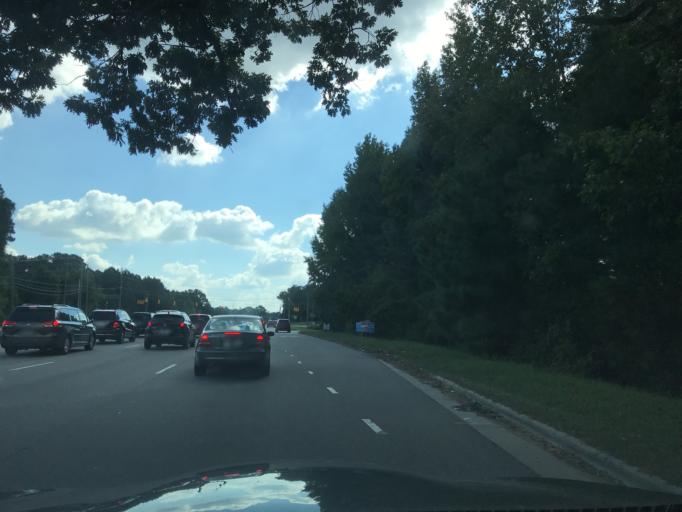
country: US
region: North Carolina
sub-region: Wake County
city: Rolesville
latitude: 35.8701
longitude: -78.5450
